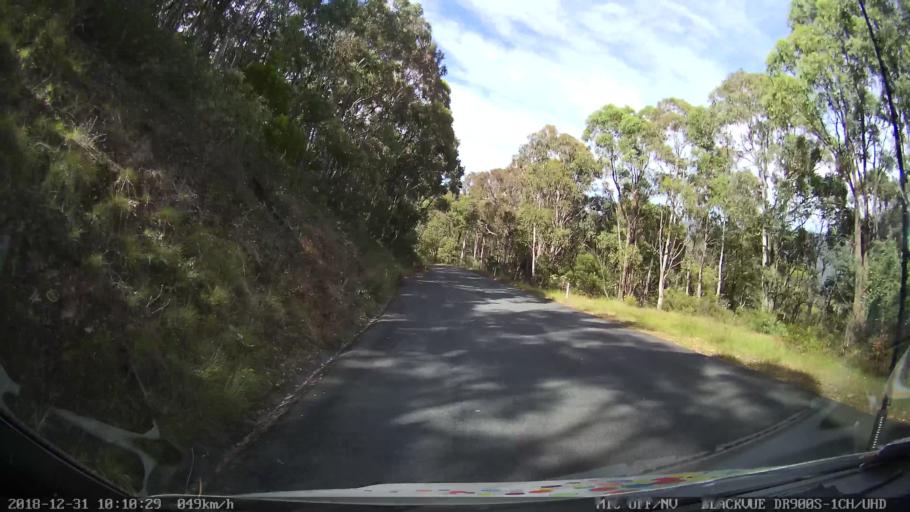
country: AU
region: New South Wales
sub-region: Snowy River
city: Jindabyne
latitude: -36.5370
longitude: 148.1695
